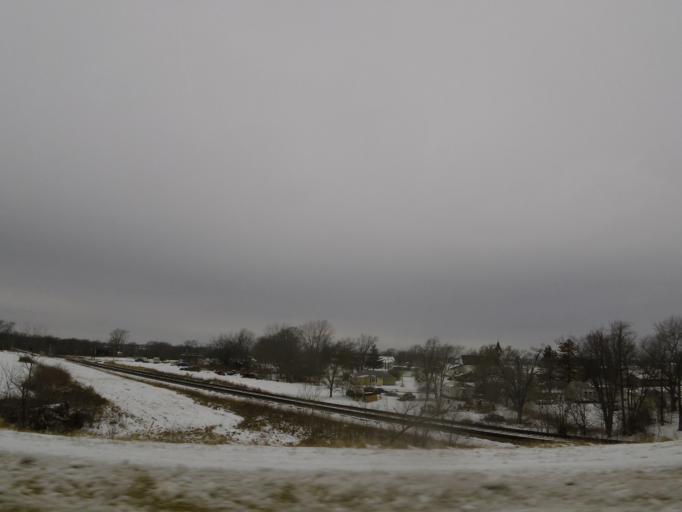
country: US
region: Illinois
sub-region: Hancock County
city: Nauvoo
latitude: 40.5313
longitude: -91.5632
